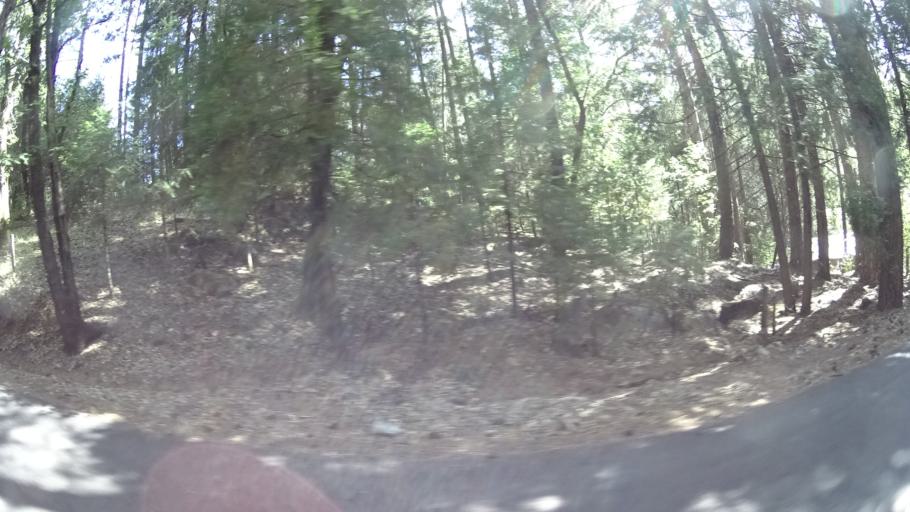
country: US
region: California
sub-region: Amador County
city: Pioneer
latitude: 38.4013
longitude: -120.5023
